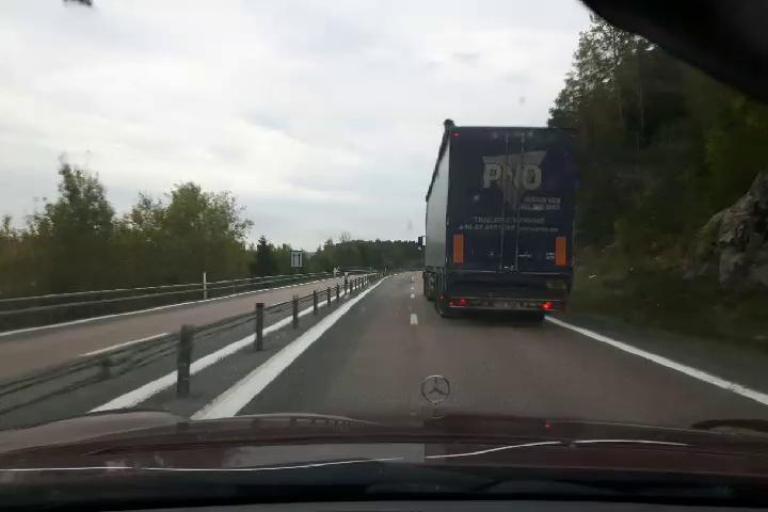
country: SE
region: Vaesternorrland
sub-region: Haernoesands Kommun
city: Haernoesand
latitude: 62.8209
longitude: 17.9699
